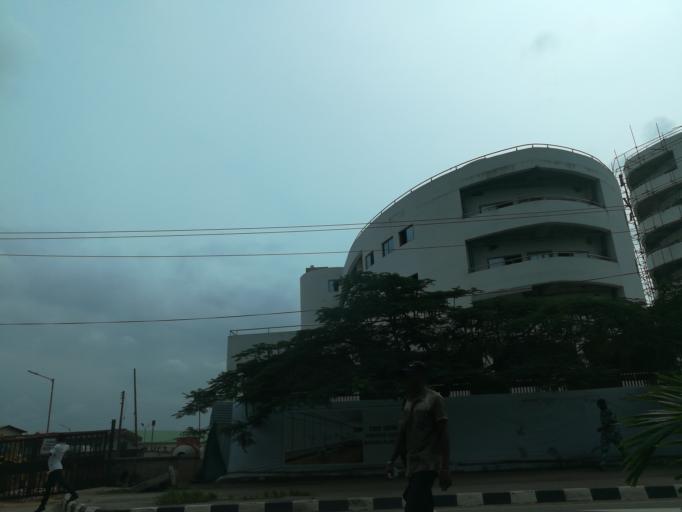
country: NG
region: Lagos
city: Ikeja
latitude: 6.6167
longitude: 3.3623
